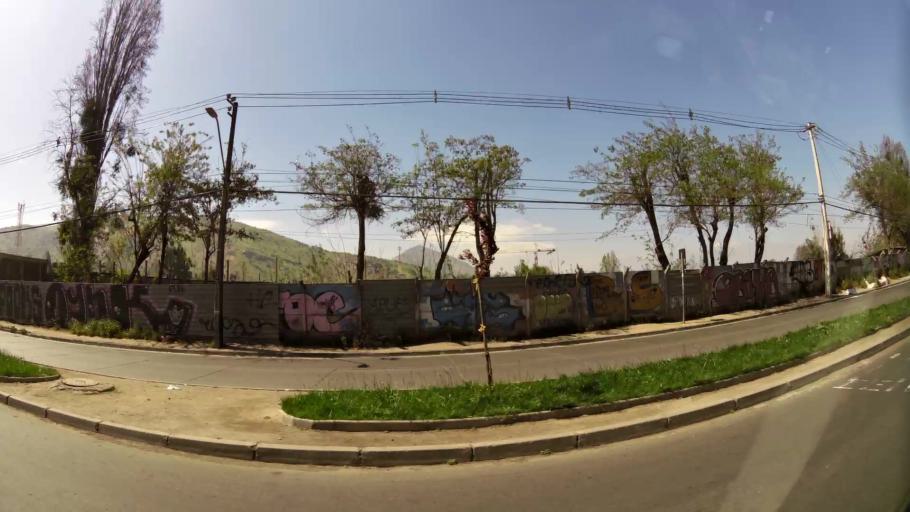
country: CL
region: Santiago Metropolitan
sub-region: Provincia de Santiago
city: Lo Prado
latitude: -33.4023
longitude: -70.7455
